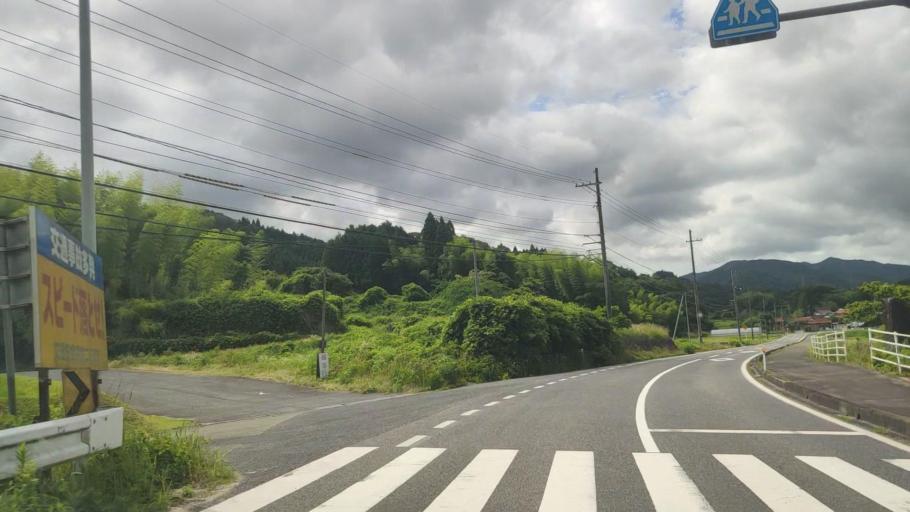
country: JP
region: Tottori
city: Yonago
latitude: 35.3071
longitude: 133.4170
